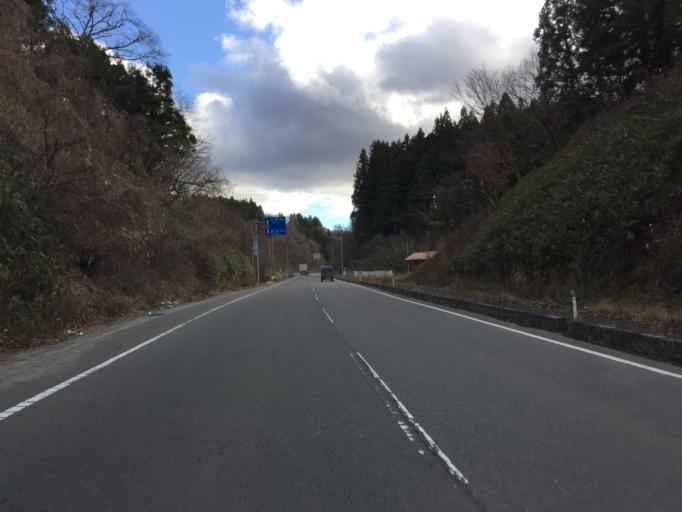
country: JP
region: Fukushima
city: Funehikimachi-funehiki
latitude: 37.5478
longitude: 140.5874
